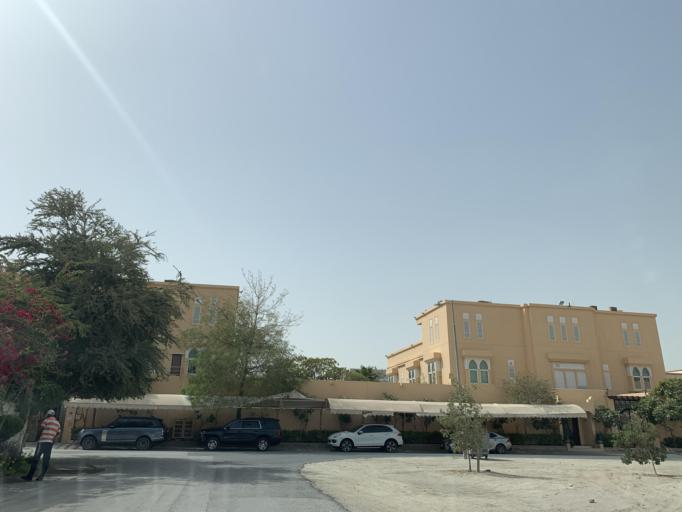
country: BH
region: Manama
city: Manama
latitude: 26.2129
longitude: 50.6146
